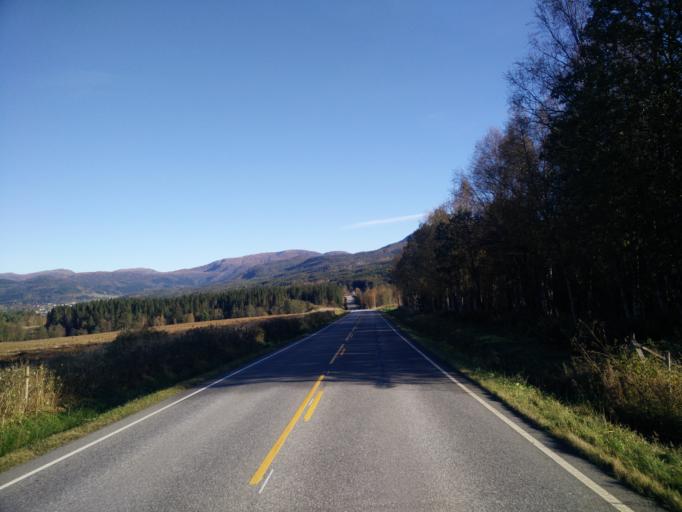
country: NO
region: More og Romsdal
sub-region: Halsa
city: Liaboen
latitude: 63.0725
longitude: 8.2680
